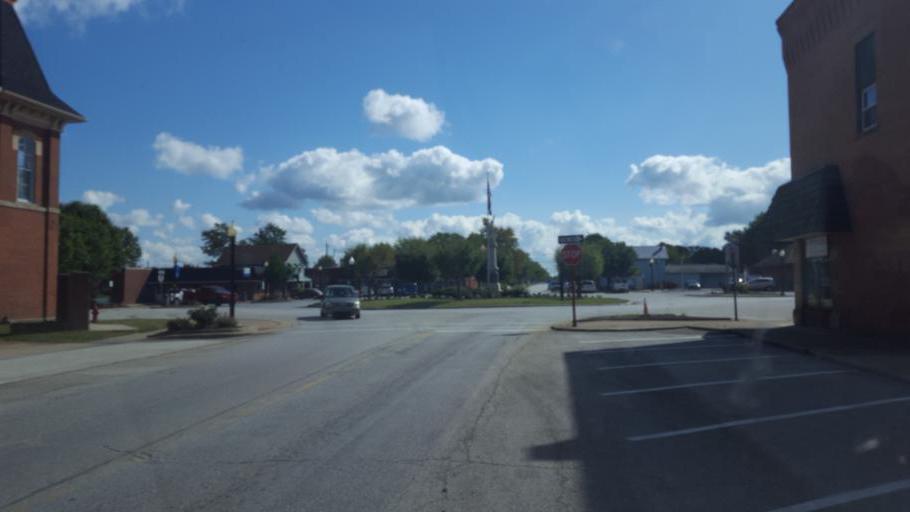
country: US
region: Ohio
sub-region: Lorain County
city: Lagrange
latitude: 41.2372
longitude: -82.1206
